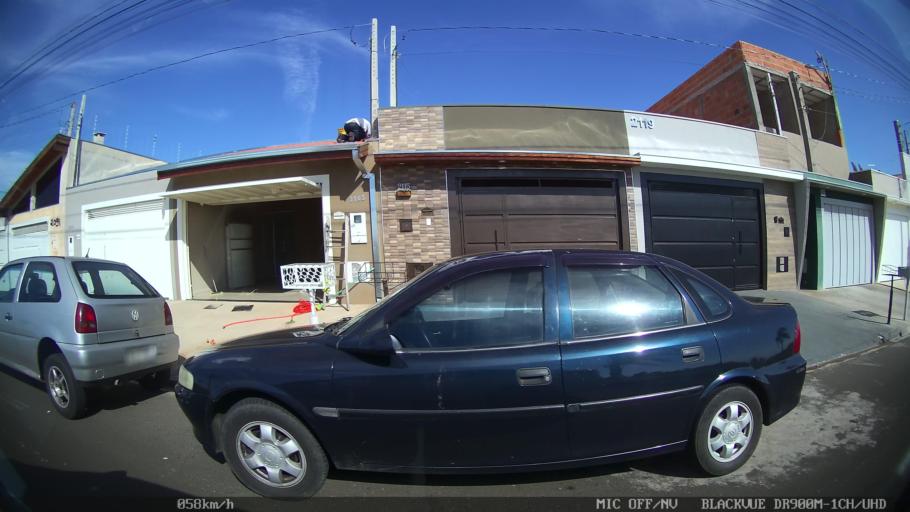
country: BR
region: Sao Paulo
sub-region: Franca
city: Franca
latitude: -20.5067
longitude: -47.4374
